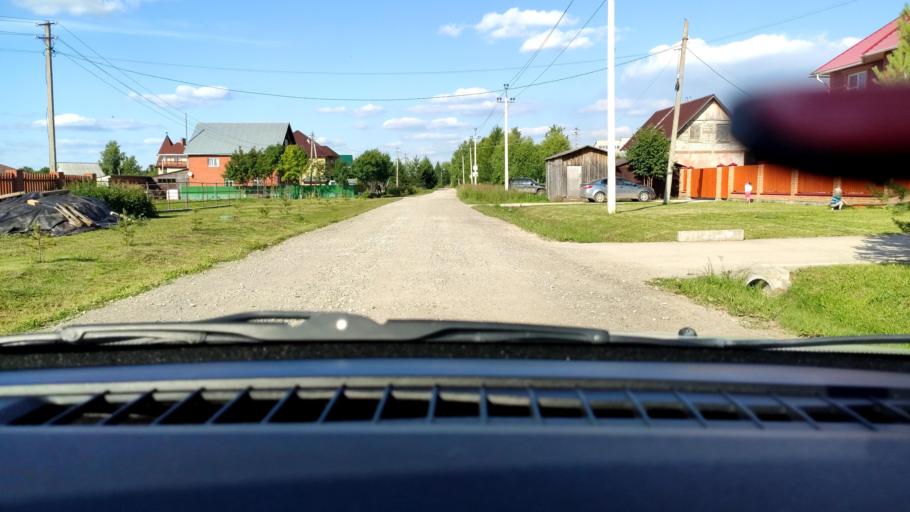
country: RU
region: Perm
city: Kultayevo
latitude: 57.8959
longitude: 55.9253
